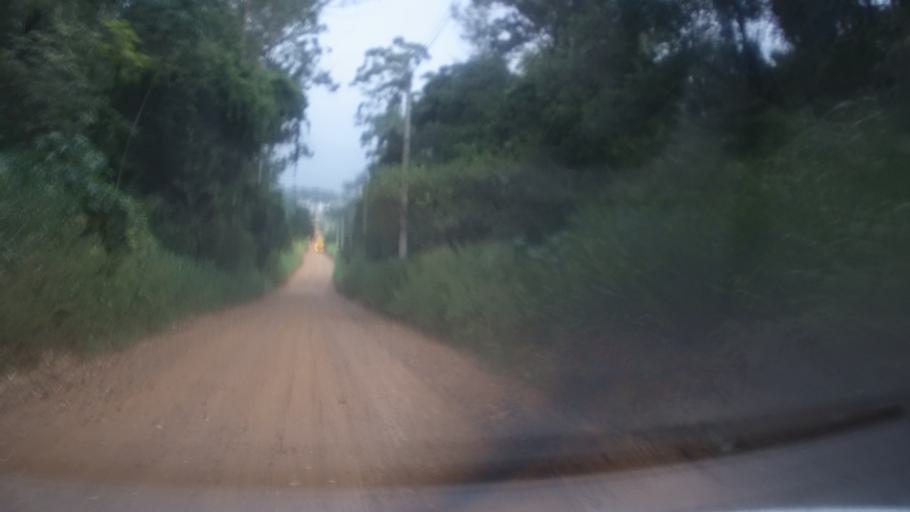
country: BR
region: Sao Paulo
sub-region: Itupeva
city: Itupeva
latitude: -23.1952
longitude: -46.9878
